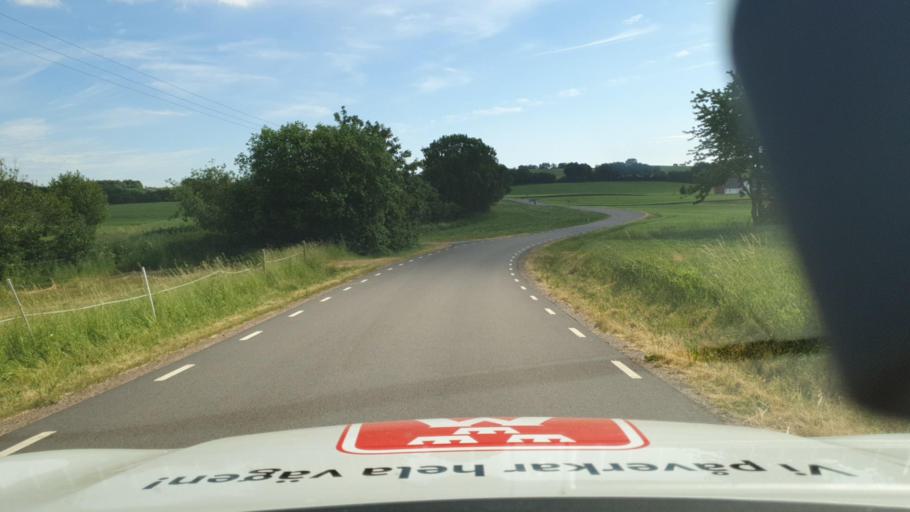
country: SE
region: Skane
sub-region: Skurups Kommun
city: Skurup
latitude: 55.5320
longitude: 13.5476
